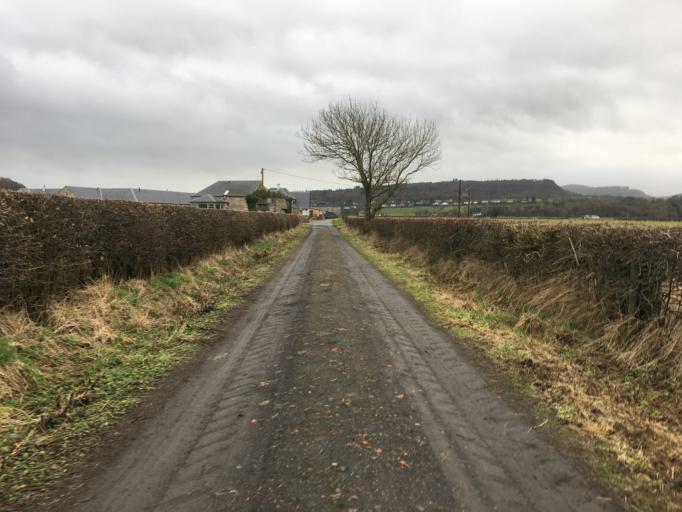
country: GB
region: Scotland
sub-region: Stirling
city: Stirling
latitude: 56.1242
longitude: -3.9760
